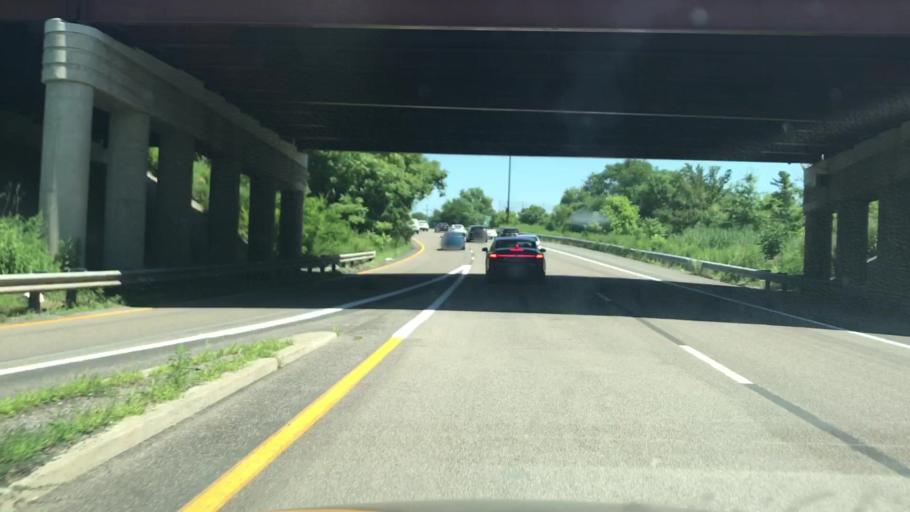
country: US
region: New Jersey
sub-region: Passaic County
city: Singac
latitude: 40.8952
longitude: -74.2509
